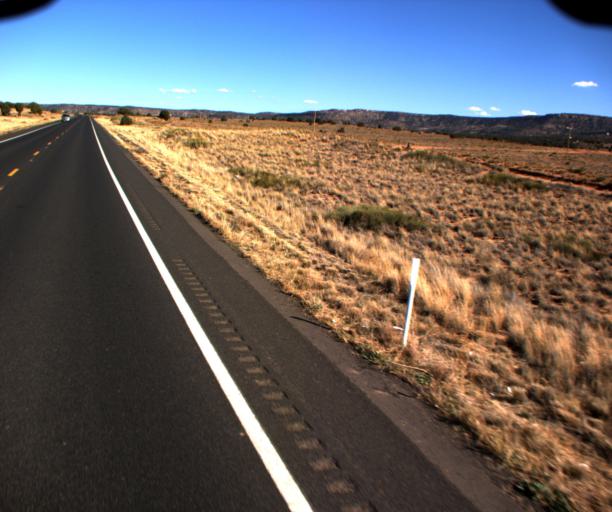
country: US
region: Arizona
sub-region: Coconino County
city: Kaibito
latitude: 36.4407
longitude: -110.7473
